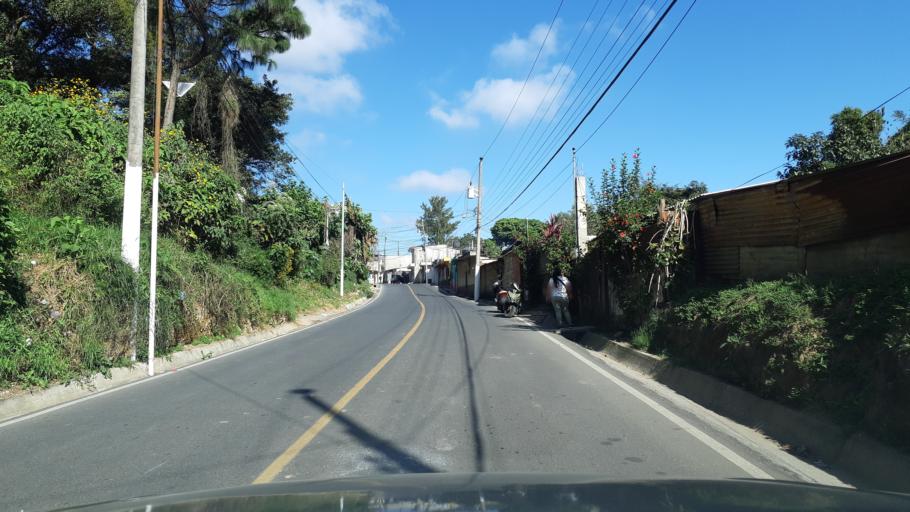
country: GT
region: Chimaltenango
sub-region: Municipio de Chimaltenango
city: Chimaltenango
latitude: 14.6538
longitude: -90.8206
